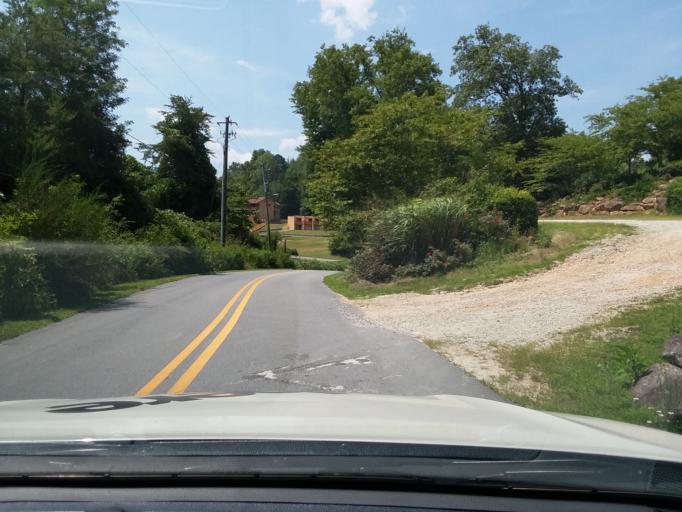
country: US
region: Georgia
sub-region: Rabun County
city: Mountain City
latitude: 34.9766
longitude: -83.3843
